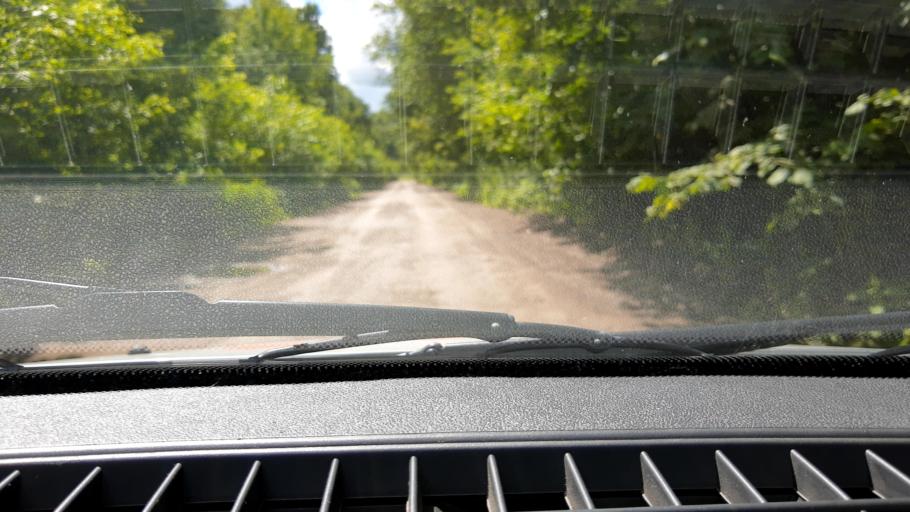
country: RU
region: Bashkortostan
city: Ufa
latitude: 54.6890
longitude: 56.0537
